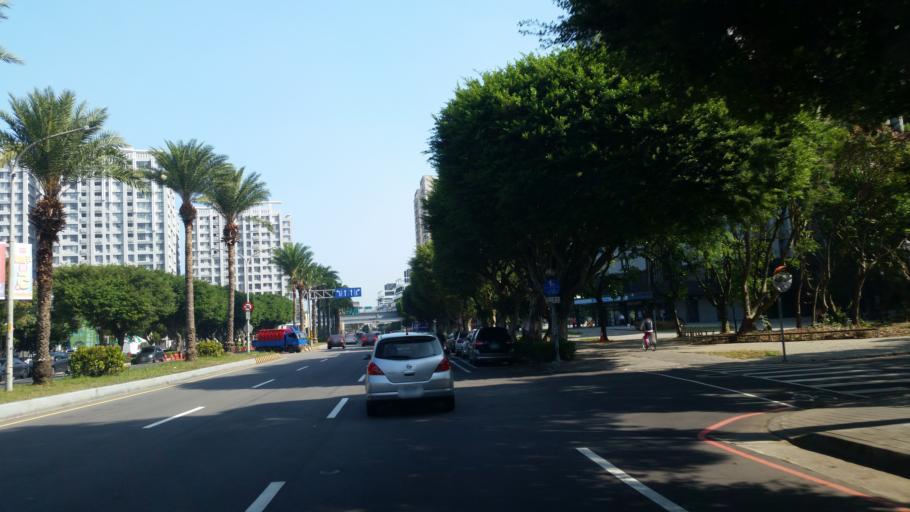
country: TW
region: Taiwan
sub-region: Taoyuan
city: Taoyuan
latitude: 25.0731
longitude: 121.3761
